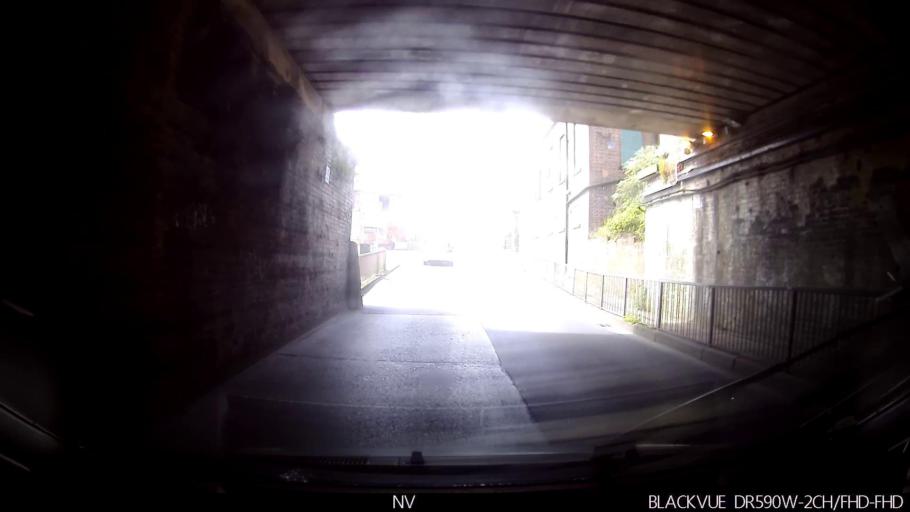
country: GB
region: England
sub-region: City of York
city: York
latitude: 53.9594
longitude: -1.0934
